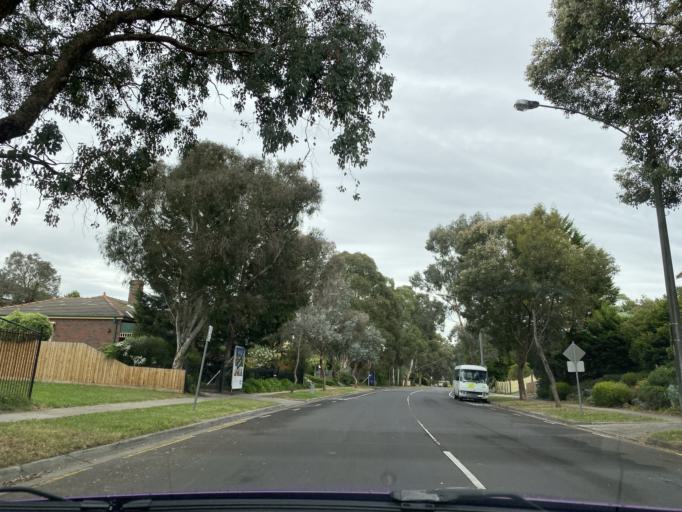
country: AU
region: Victoria
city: Saint Helena
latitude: -37.6981
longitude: 145.1347
